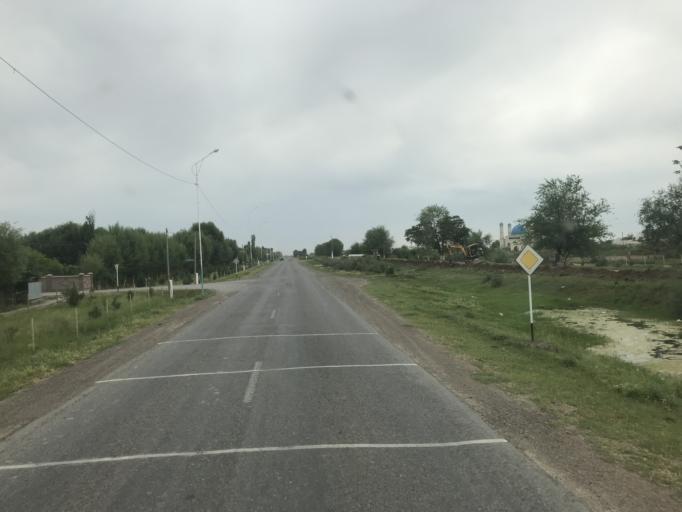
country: KZ
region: Ongtustik Qazaqstan
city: Asykata
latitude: 40.9318
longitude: 68.4078
